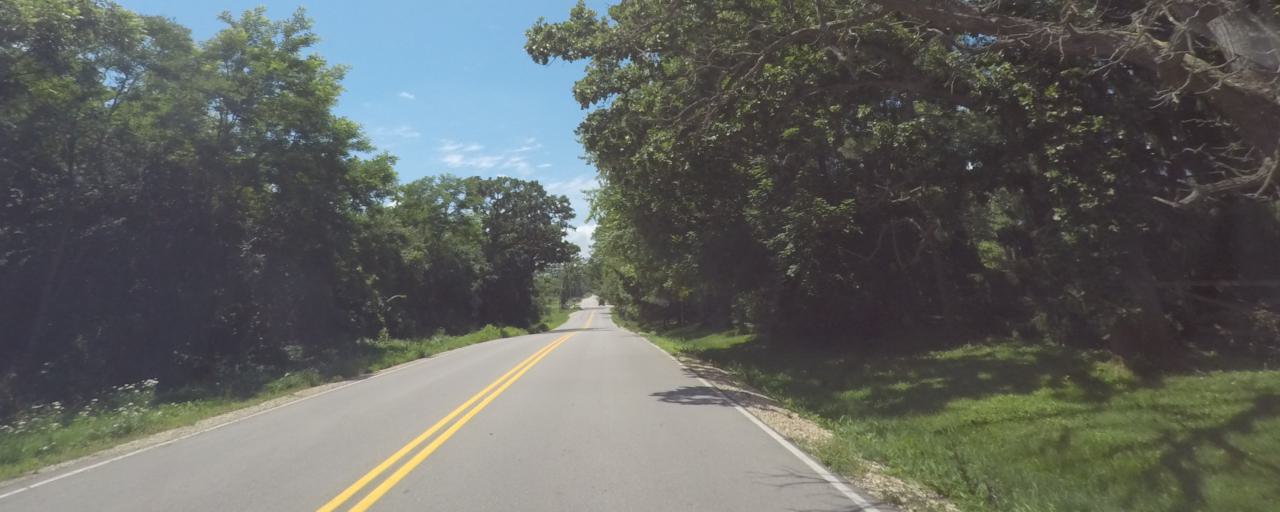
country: US
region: Wisconsin
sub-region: Waukesha County
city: Dousman
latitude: 42.9539
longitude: -88.4759
